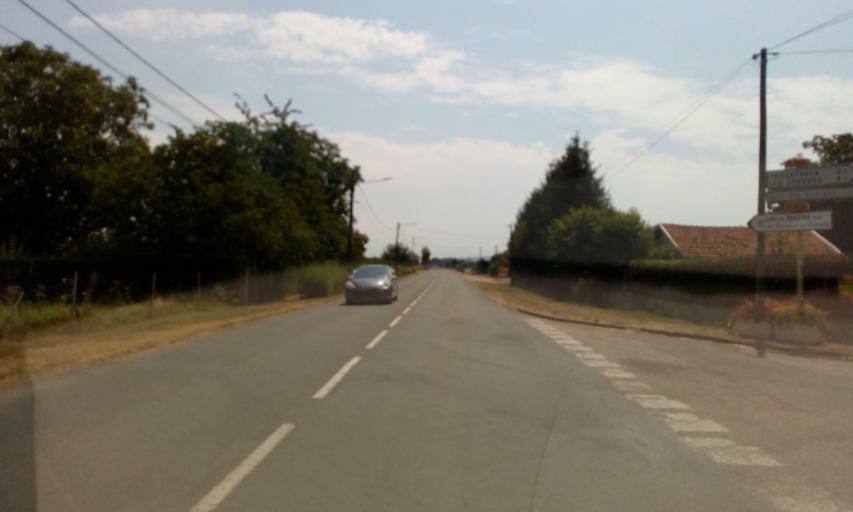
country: FR
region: Lorraine
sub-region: Departement de la Meuse
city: Etain
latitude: 49.0933
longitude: 5.6261
